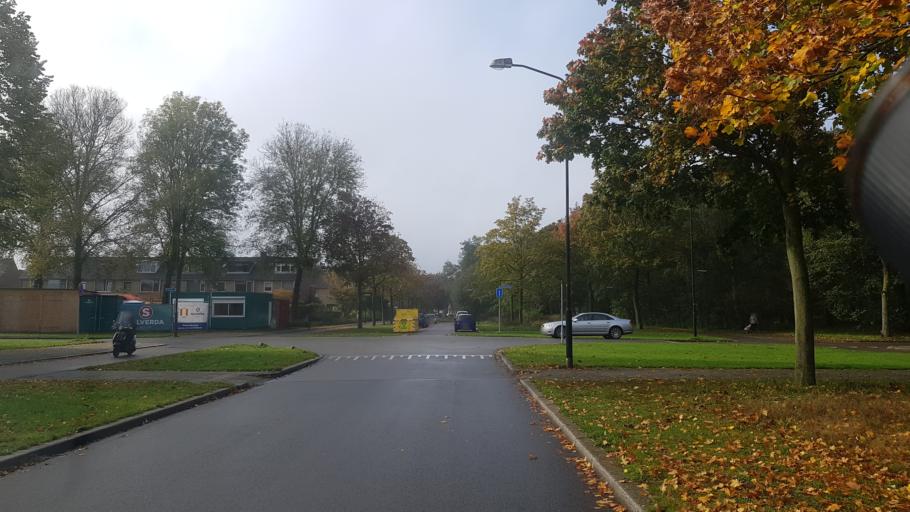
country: NL
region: Gelderland
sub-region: Gemeente Apeldoorn
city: Apeldoorn
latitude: 52.2190
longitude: 5.9862
